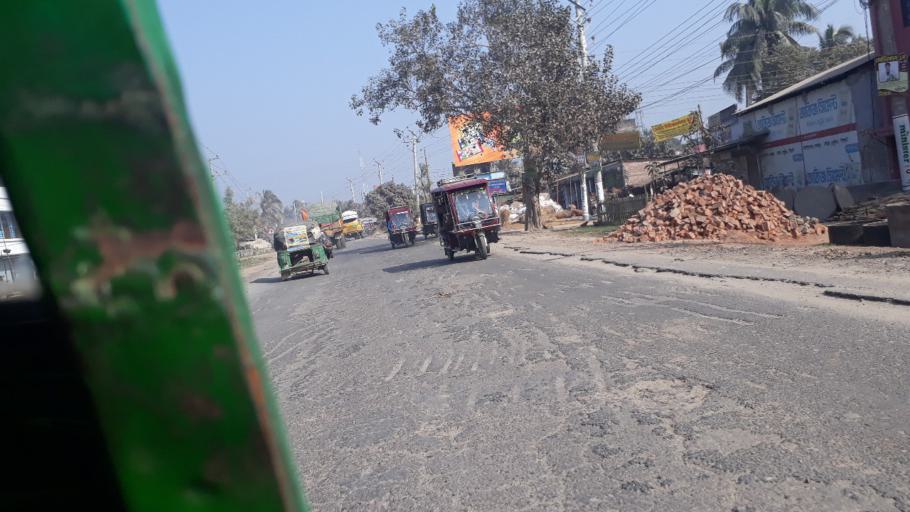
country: BD
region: Khulna
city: Kushtia
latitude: 23.8854
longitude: 89.1046
